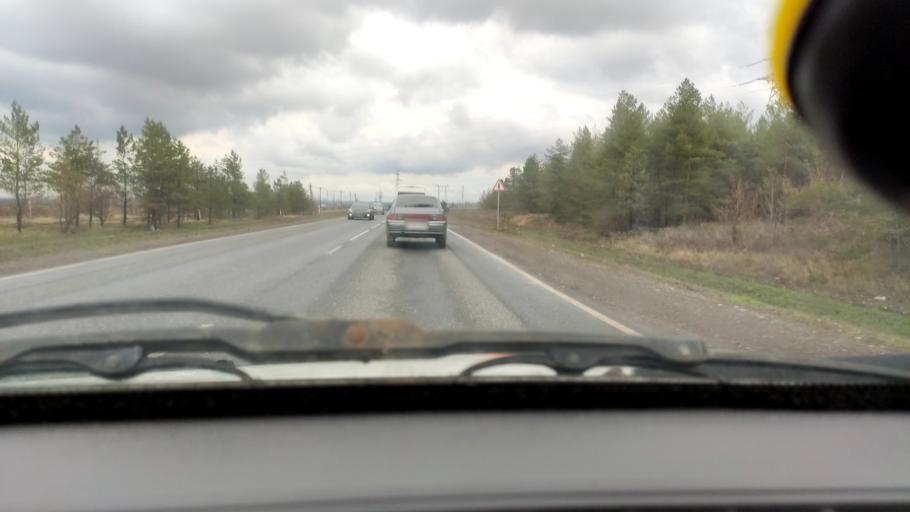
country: RU
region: Samara
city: Zhigulevsk
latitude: 53.5704
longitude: 49.5513
